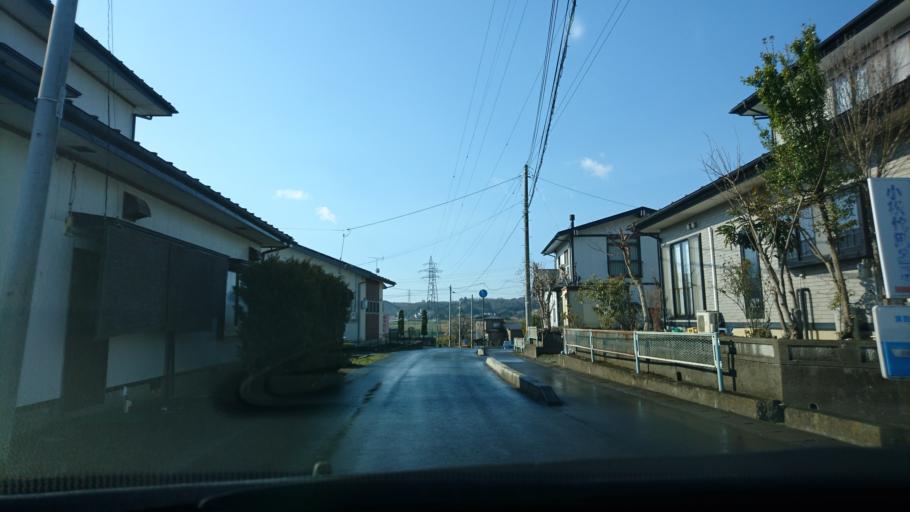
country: JP
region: Iwate
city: Ichinoseki
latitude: 38.9868
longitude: 141.1115
